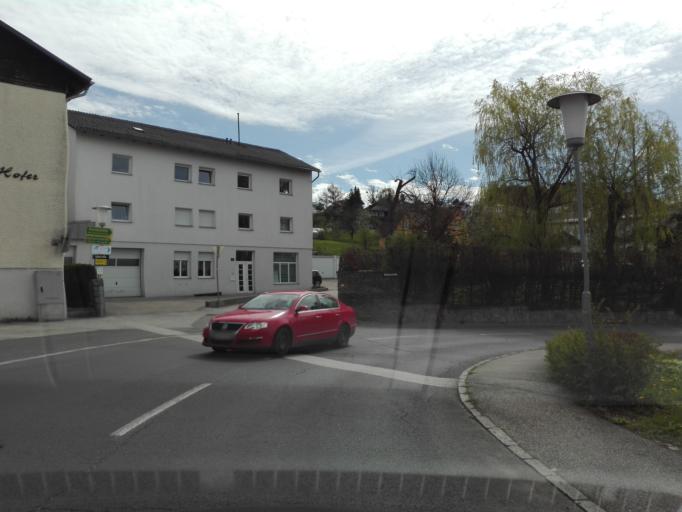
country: AT
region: Upper Austria
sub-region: Politischer Bezirk Urfahr-Umgebung
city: Gramastetten
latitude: 48.3799
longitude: 14.1931
